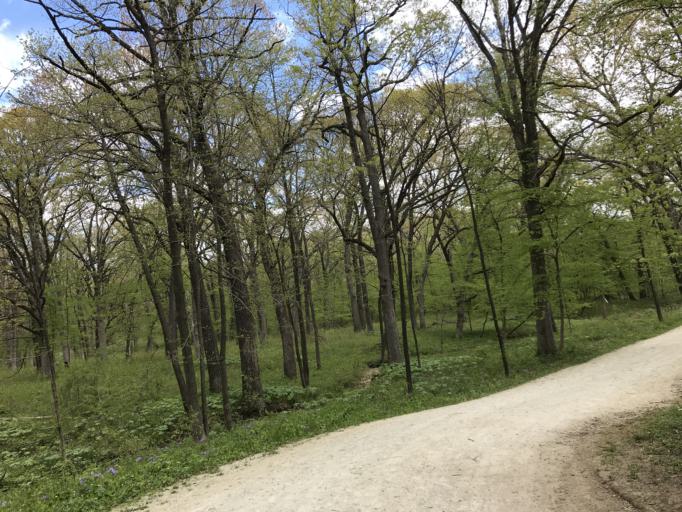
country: US
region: Illinois
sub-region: DuPage County
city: Woodridge
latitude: 41.7380
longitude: -88.0783
